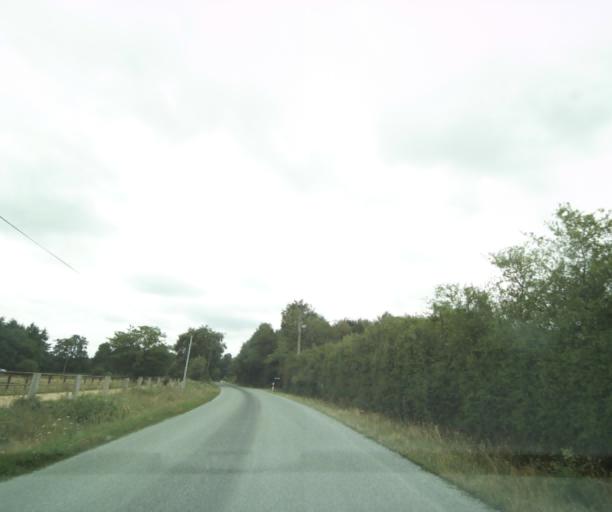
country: FR
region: Pays de la Loire
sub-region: Departement de Maine-et-Loire
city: Durtal
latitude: 47.7094
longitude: -0.2686
